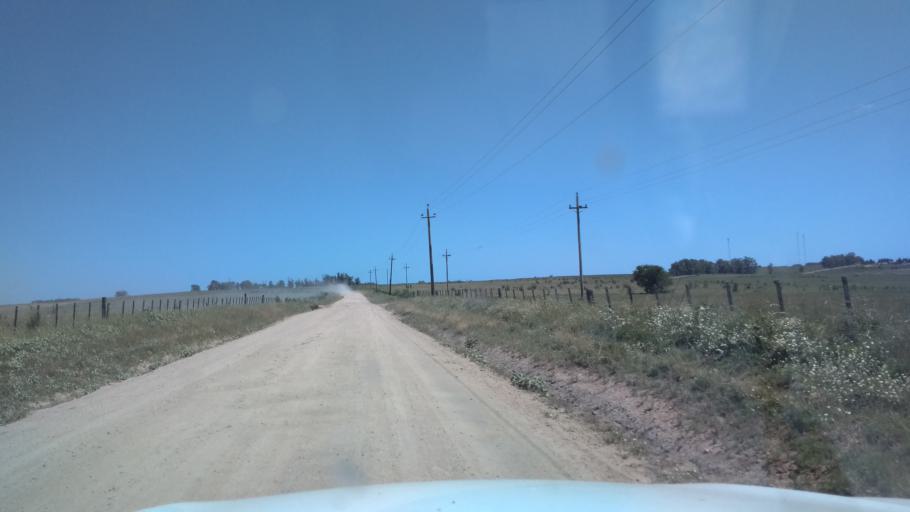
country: UY
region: Florida
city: Casupa
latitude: -34.0555
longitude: -55.8921
